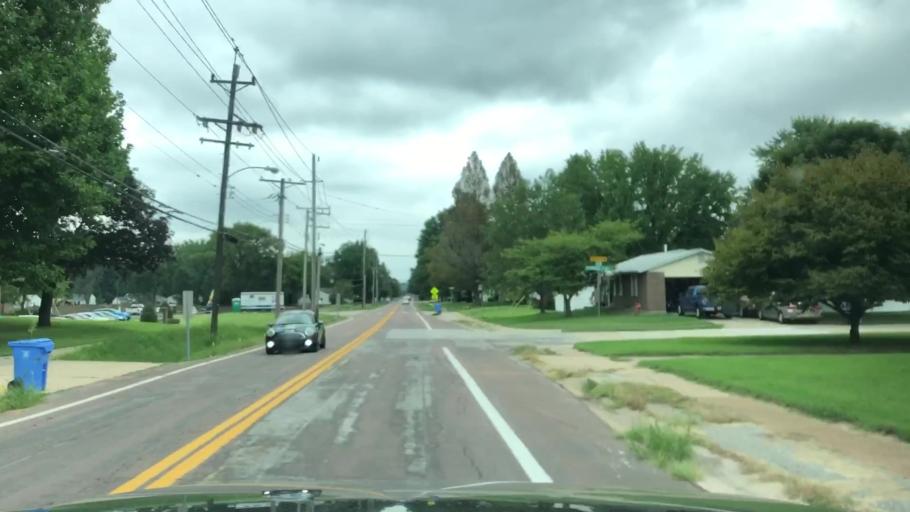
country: US
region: Missouri
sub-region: Saint Louis County
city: Florissant
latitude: 38.8046
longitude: -90.3518
